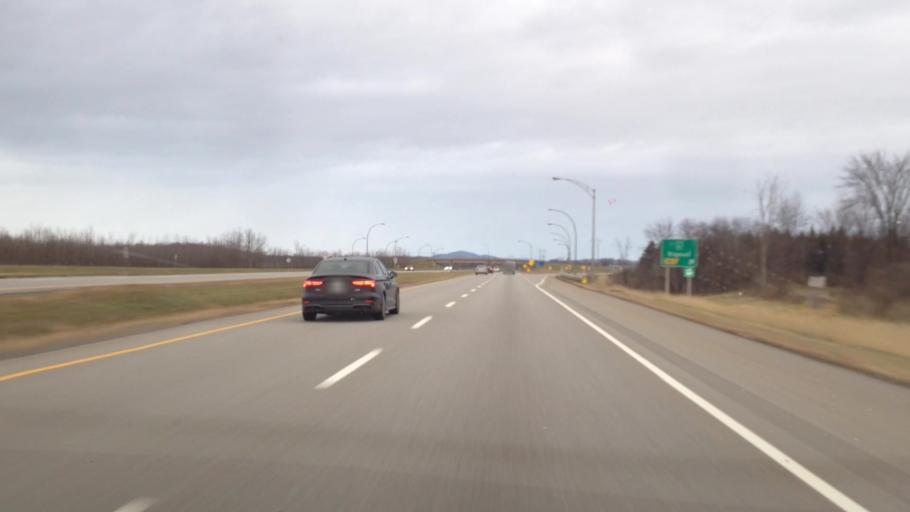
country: CA
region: Quebec
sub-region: Monteregie
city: Rigaud
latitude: 45.4872
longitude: -74.3211
